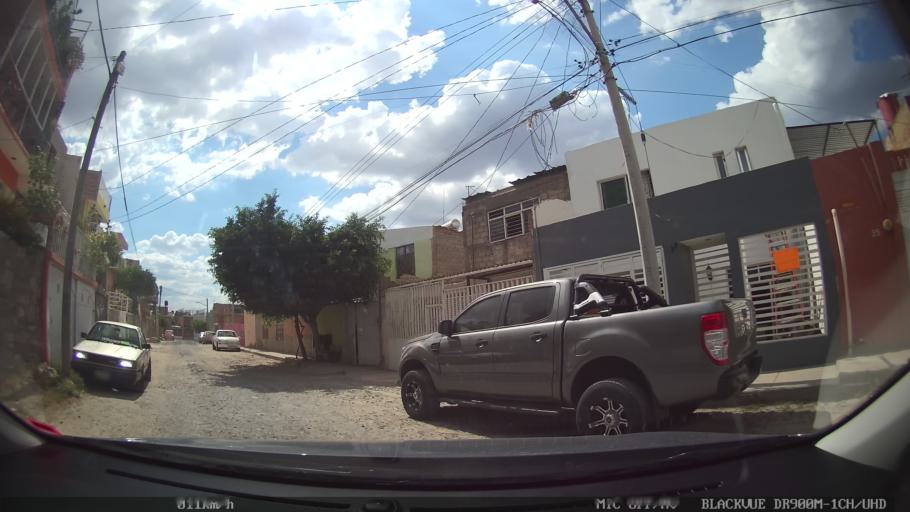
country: MX
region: Jalisco
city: Tlaquepaque
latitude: 20.6853
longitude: -103.2606
